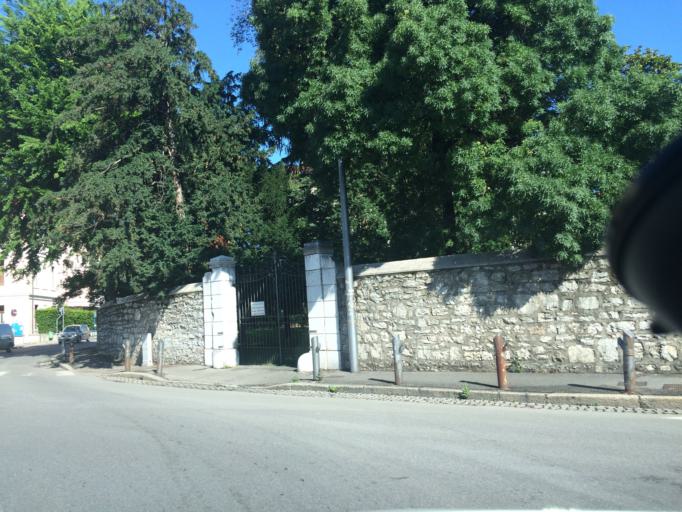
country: IT
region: Lombardy
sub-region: Provincia di Brescia
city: Brescia
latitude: 45.5316
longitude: 10.2083
